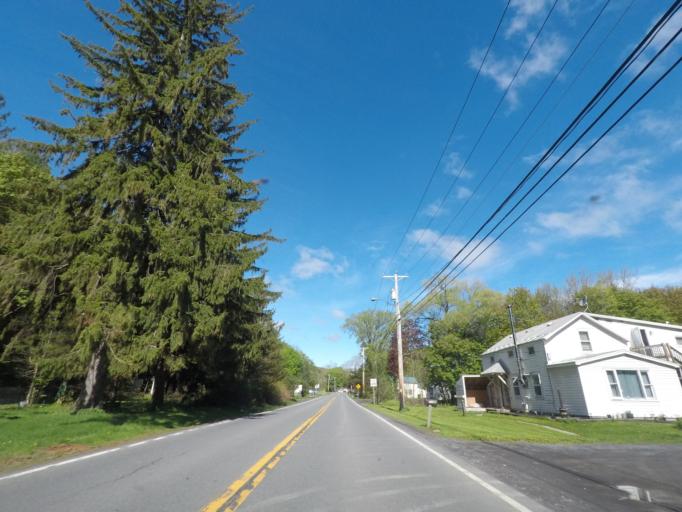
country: US
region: New York
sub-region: Albany County
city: Ravena
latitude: 42.4686
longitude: -73.8860
